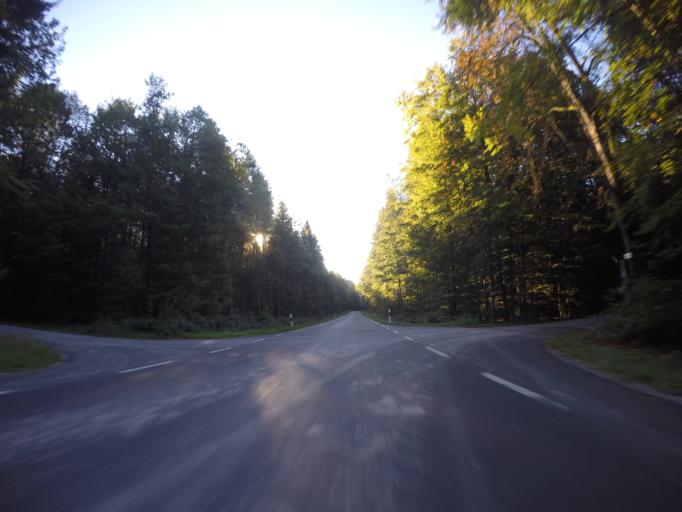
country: DE
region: Bavaria
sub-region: Regierungsbezirk Unterfranken
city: Altenbuch
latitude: 49.8579
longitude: 9.4278
